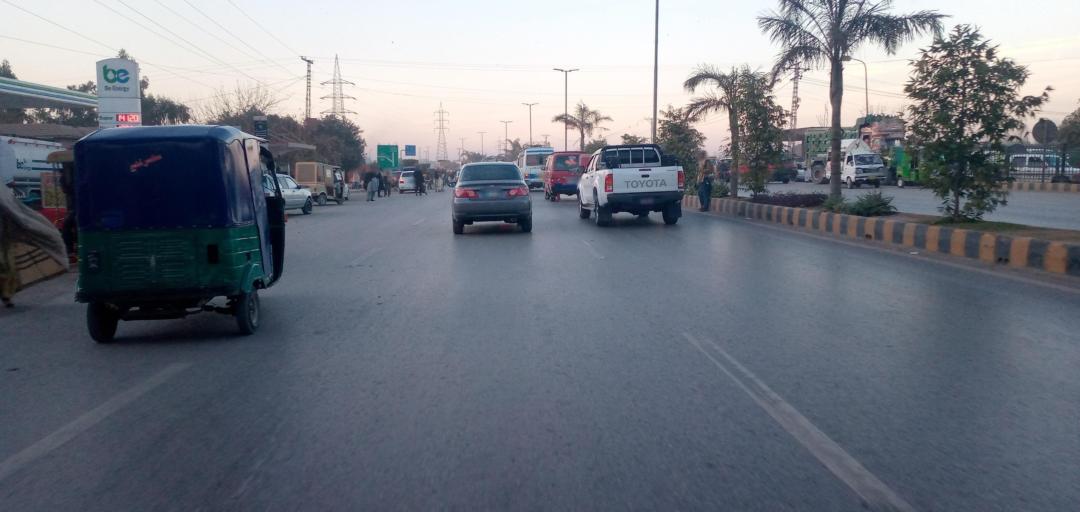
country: PK
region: Khyber Pakhtunkhwa
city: Peshawar
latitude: 34.0239
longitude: 71.6205
